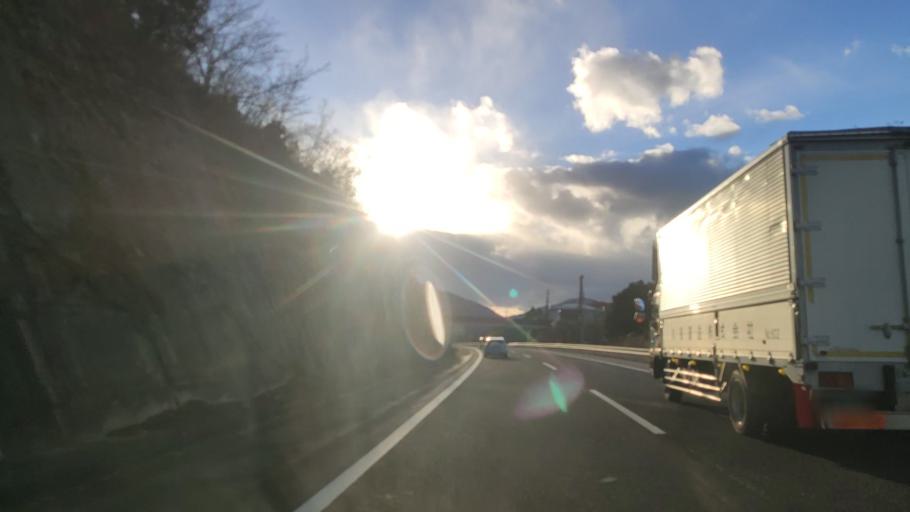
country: JP
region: Ehime
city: Saijo
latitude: 33.8708
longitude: 133.0627
